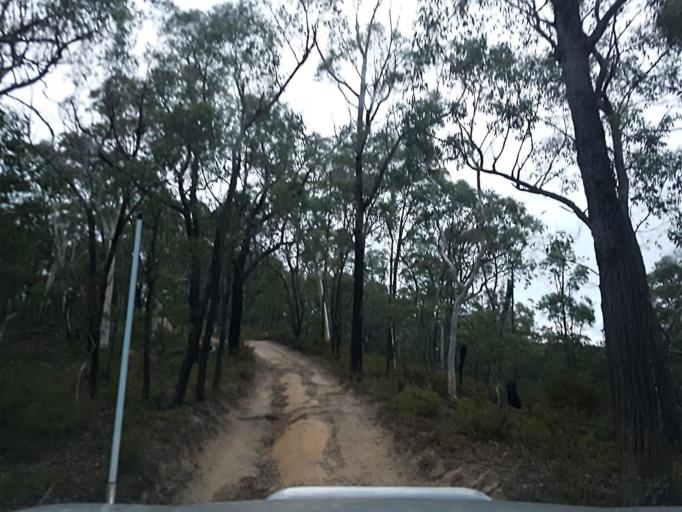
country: AU
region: New South Wales
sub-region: Snowy River
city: Jindabyne
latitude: -36.8563
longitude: 148.2316
